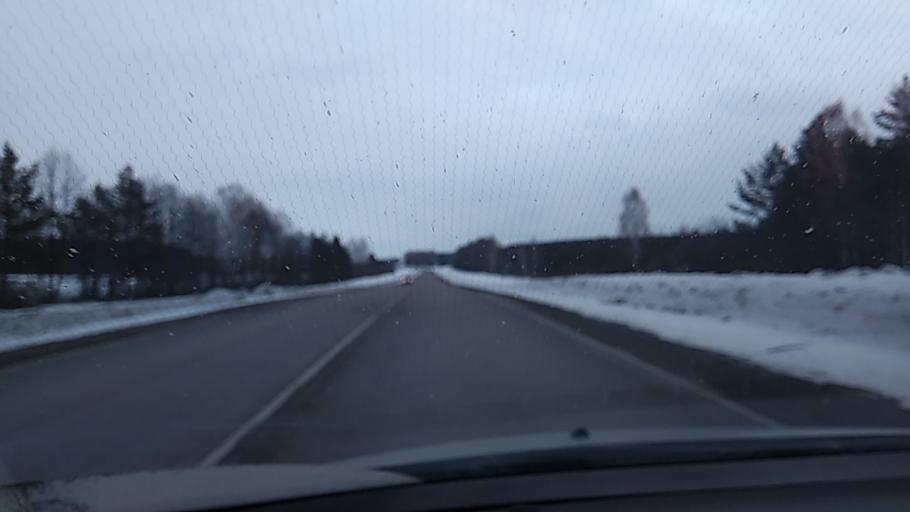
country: RU
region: Sverdlovsk
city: Dvurechensk
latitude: 56.6802
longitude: 61.1270
